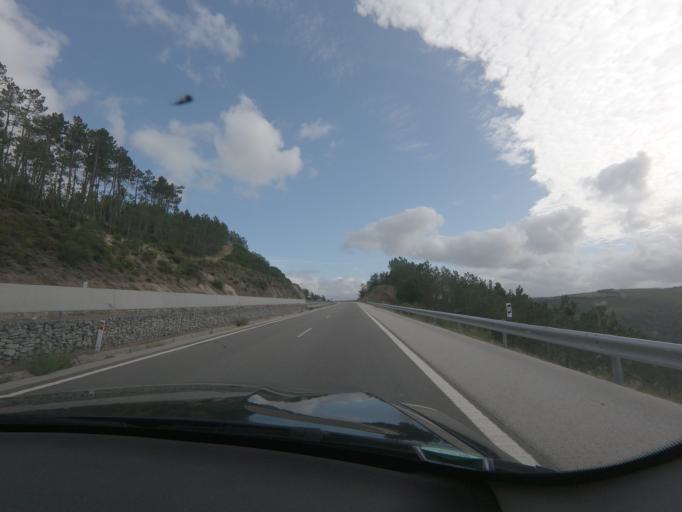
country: PT
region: Viseu
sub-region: Lamego
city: Lamego
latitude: 41.0465
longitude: -7.8598
